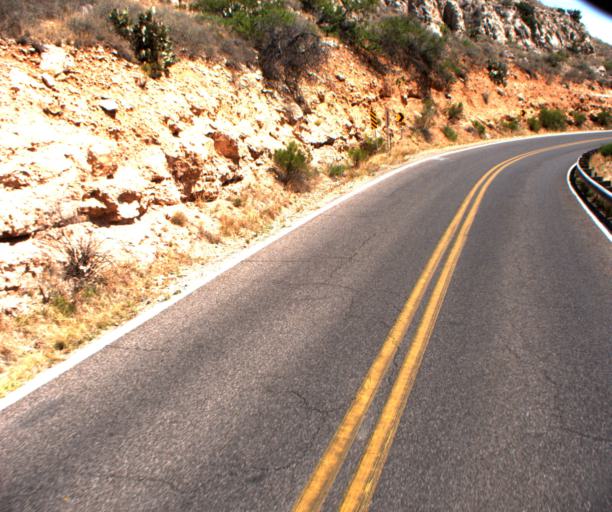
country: US
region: Arizona
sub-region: Yavapai County
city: Clarkdale
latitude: 34.7554
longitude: -112.0905
